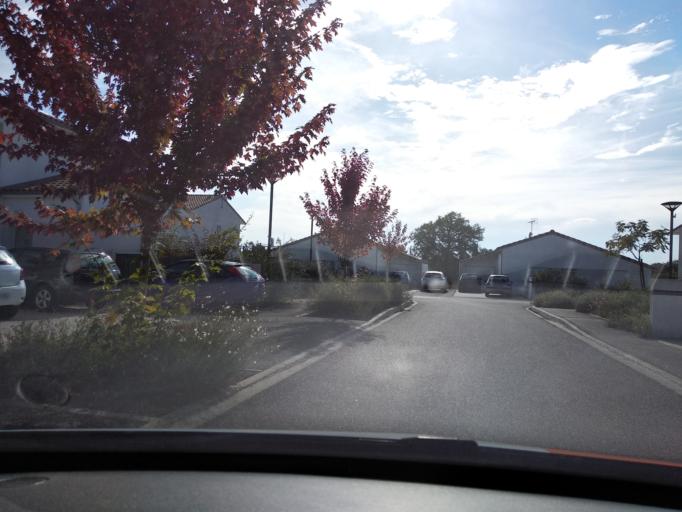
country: FR
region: Midi-Pyrenees
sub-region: Departement du Tarn-et-Garonne
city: Montauban
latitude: 44.0441
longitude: 1.3306
